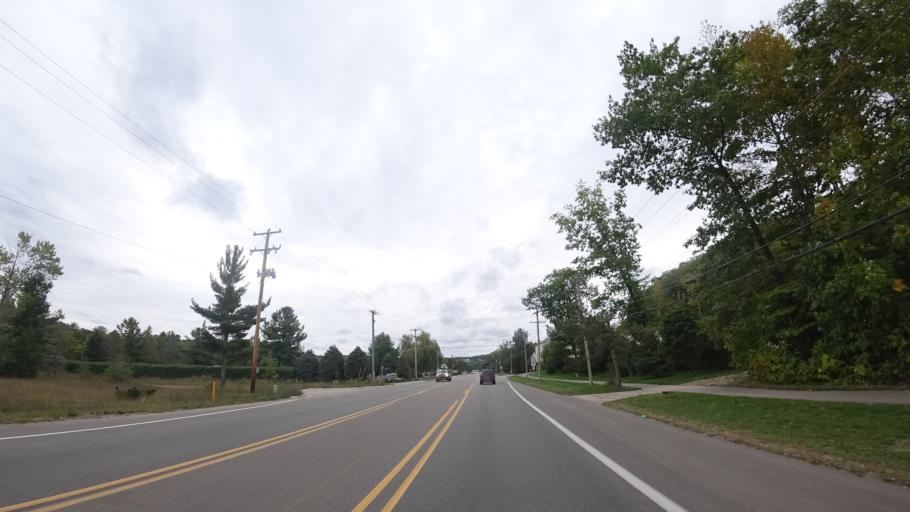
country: US
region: Michigan
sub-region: Emmet County
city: Petoskey
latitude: 45.4057
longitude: -84.9021
